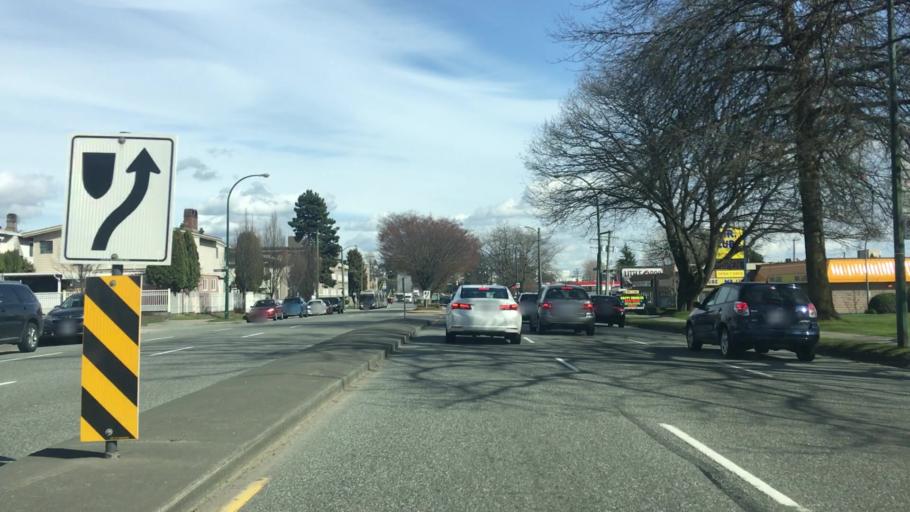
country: CA
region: British Columbia
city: Vancouver
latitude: 49.2110
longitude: -123.0949
